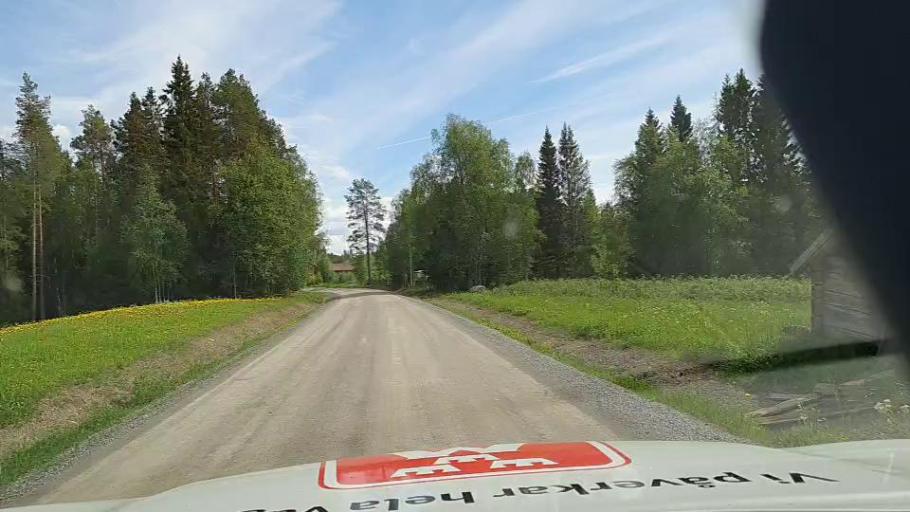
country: SE
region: Jaemtland
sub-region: OEstersunds Kommun
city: Brunflo
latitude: 63.0046
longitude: 14.7939
